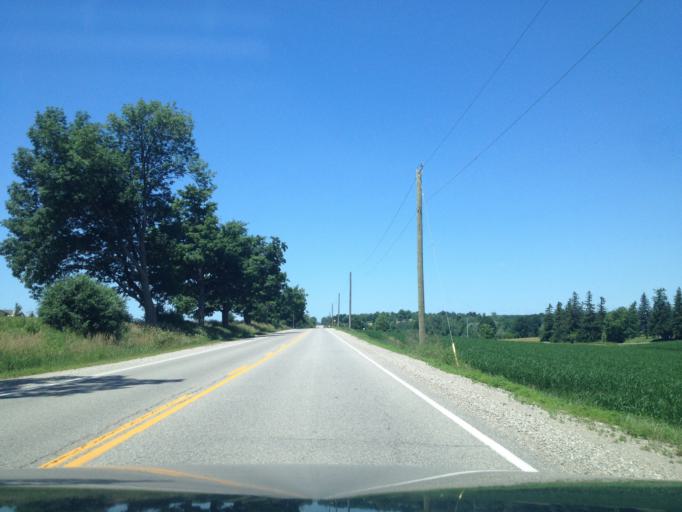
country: CA
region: Ontario
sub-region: Wellington County
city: Guelph
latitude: 43.6251
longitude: -80.2274
